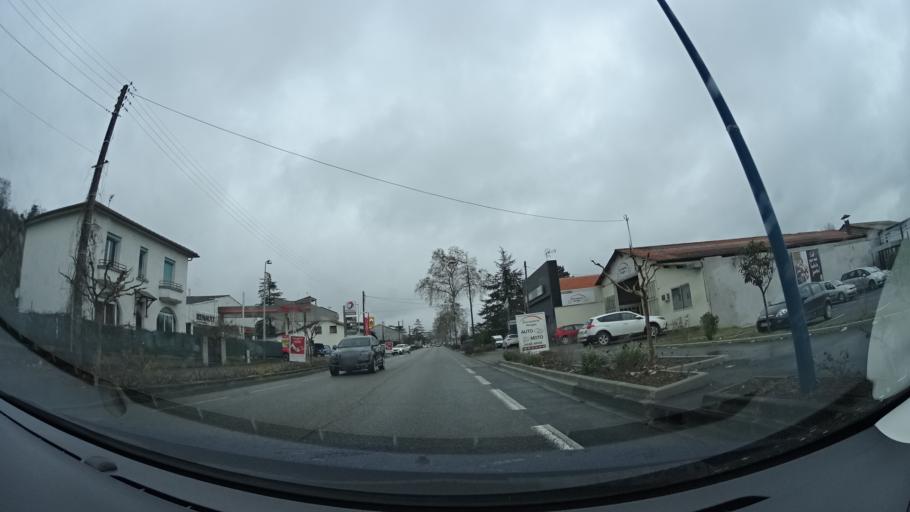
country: FR
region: Midi-Pyrenees
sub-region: Departement du Tarn-et-Garonne
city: Moissac
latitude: 44.1100
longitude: 1.1016
